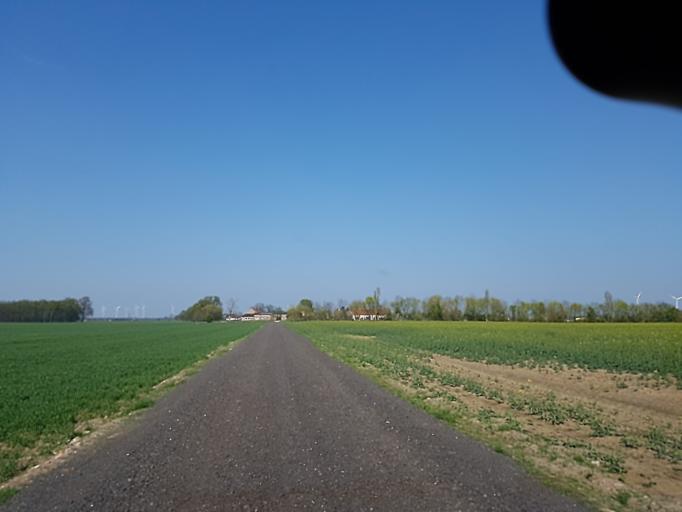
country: DE
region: Brandenburg
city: Falkenberg
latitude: 51.5222
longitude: 13.2888
